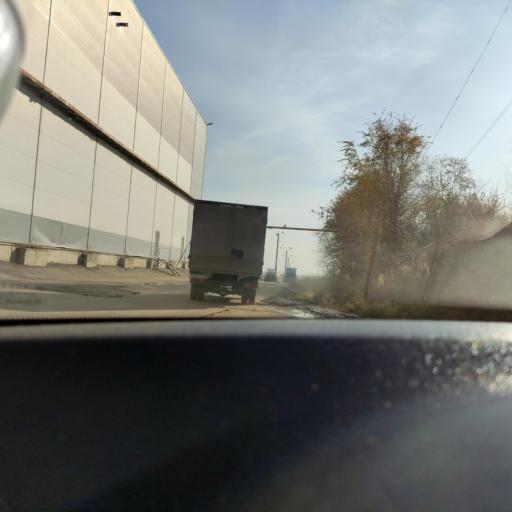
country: RU
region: Samara
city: Petra-Dubrava
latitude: 53.2745
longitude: 50.2723
